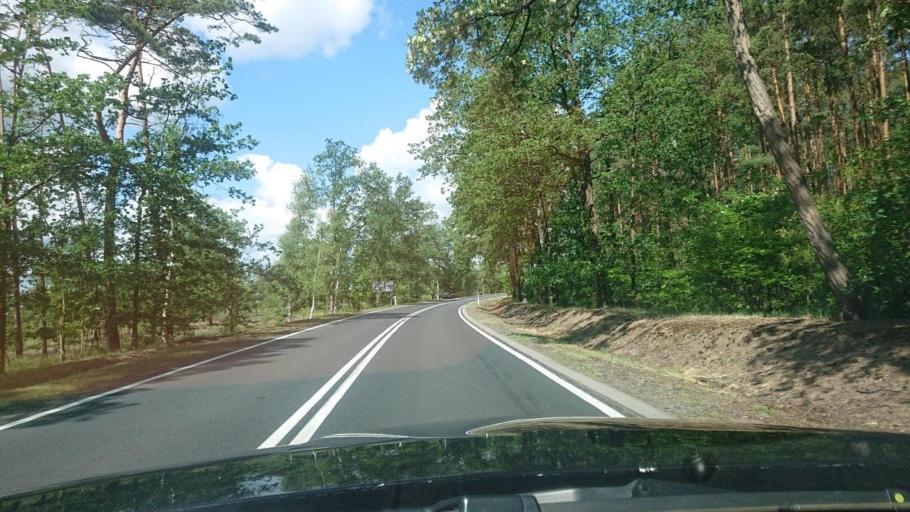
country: PL
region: Lubusz
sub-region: Powiat zaganski
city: Szprotawa
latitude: 51.5470
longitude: 15.5993
